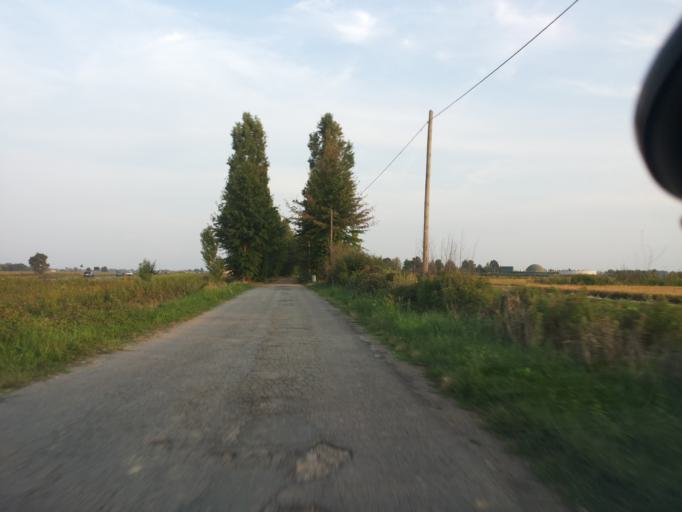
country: IT
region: Piedmont
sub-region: Provincia di Vercelli
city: Casanova Elvo
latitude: 45.4130
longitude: 8.3202
